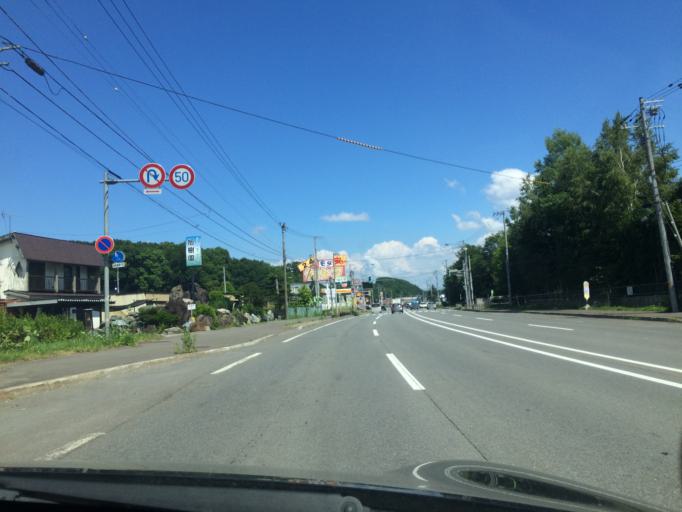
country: JP
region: Hokkaido
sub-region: Asahikawa-shi
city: Asahikawa
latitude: 43.7687
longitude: 142.2851
